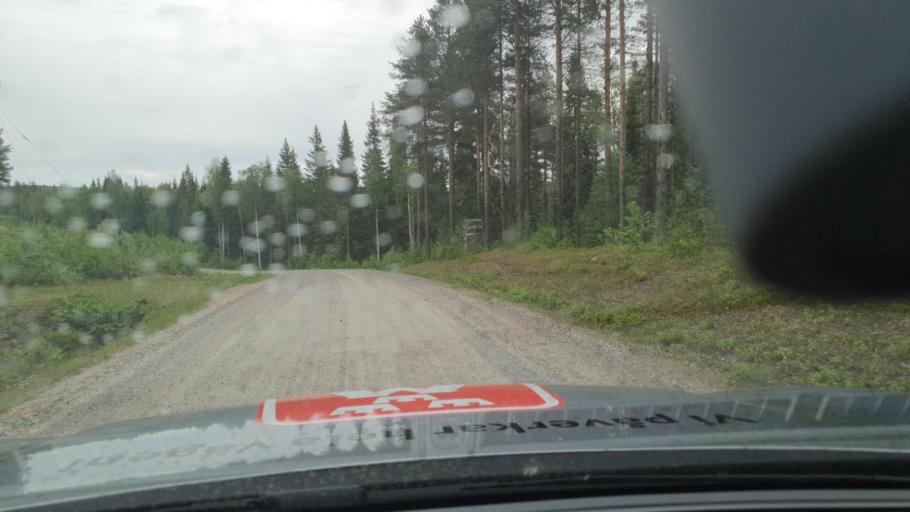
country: SE
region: Norrbotten
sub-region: Kalix Kommun
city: Rolfs
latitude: 66.0213
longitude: 23.0943
